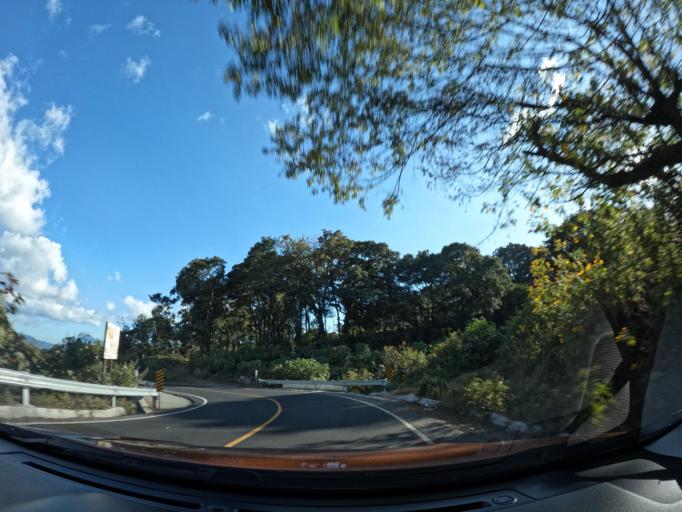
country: GT
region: Sacatepequez
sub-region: Municipio de Santa Maria de Jesus
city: Santa Maria de Jesus
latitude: 14.4812
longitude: -90.7019
